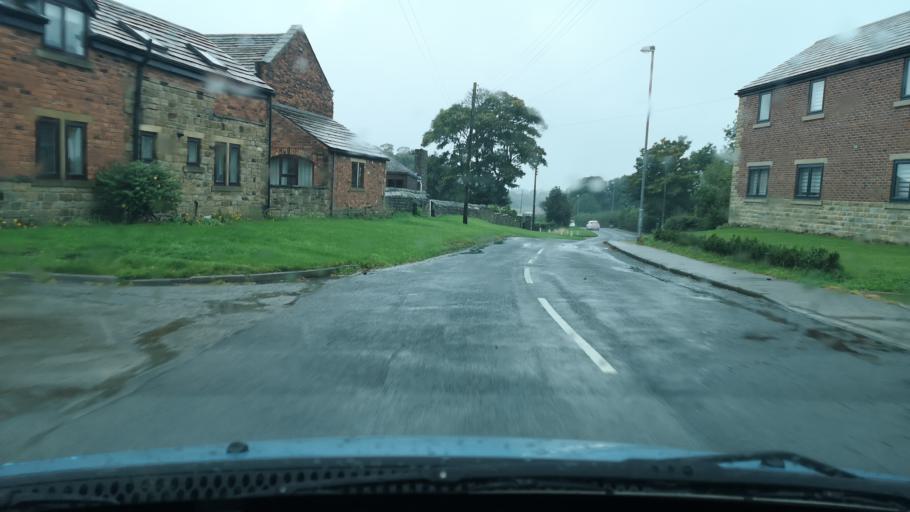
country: GB
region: England
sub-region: City and Borough of Wakefield
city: Sharlston
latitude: 53.6636
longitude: -1.4089
